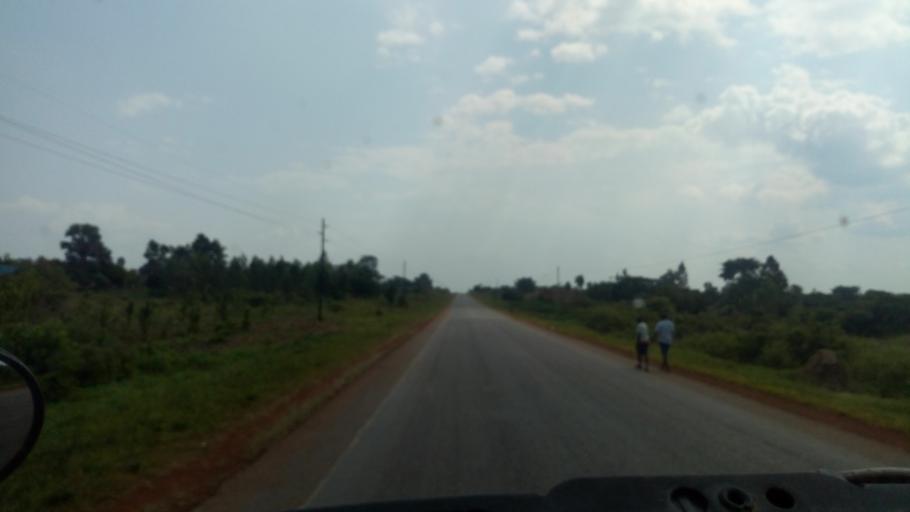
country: UG
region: Northern Region
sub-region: Oyam District
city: Oyam
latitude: 2.2174
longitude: 32.3941
